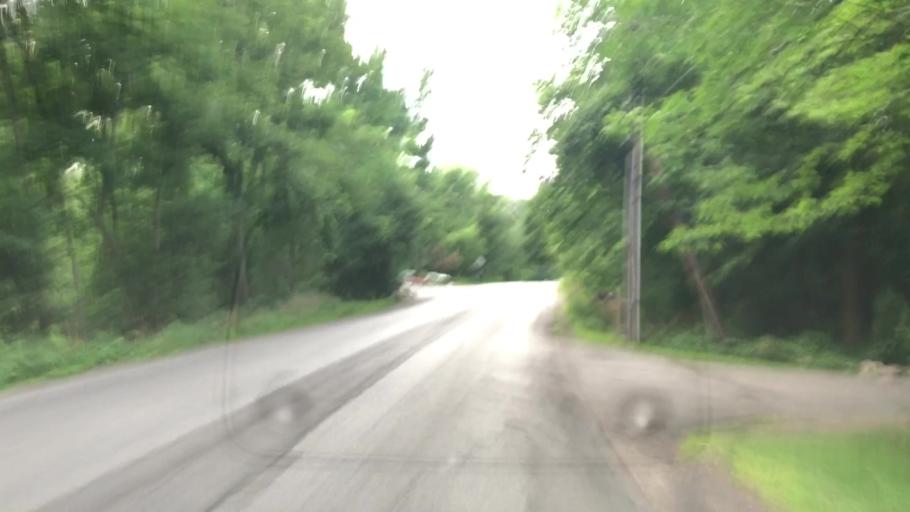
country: US
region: New York
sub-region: Erie County
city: East Aurora
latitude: 42.7835
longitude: -78.6045
